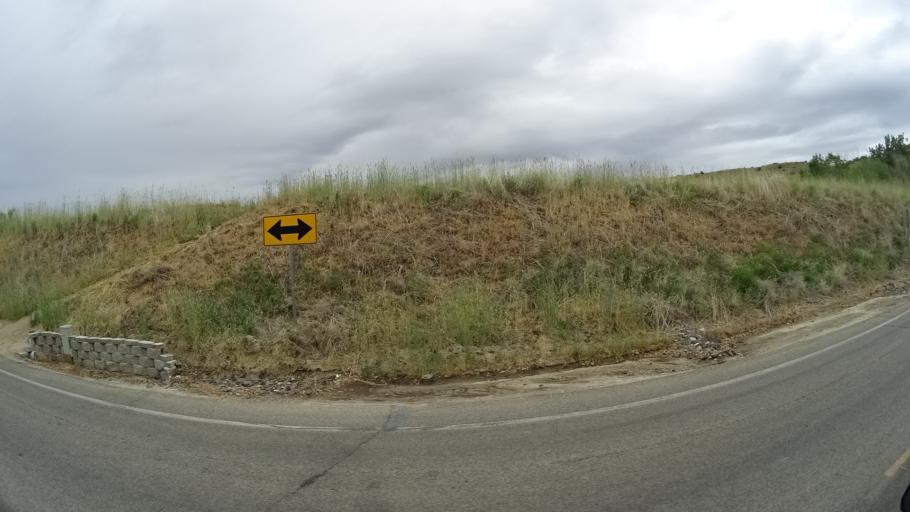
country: US
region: Idaho
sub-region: Ada County
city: Boise
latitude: 43.6151
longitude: -116.1835
